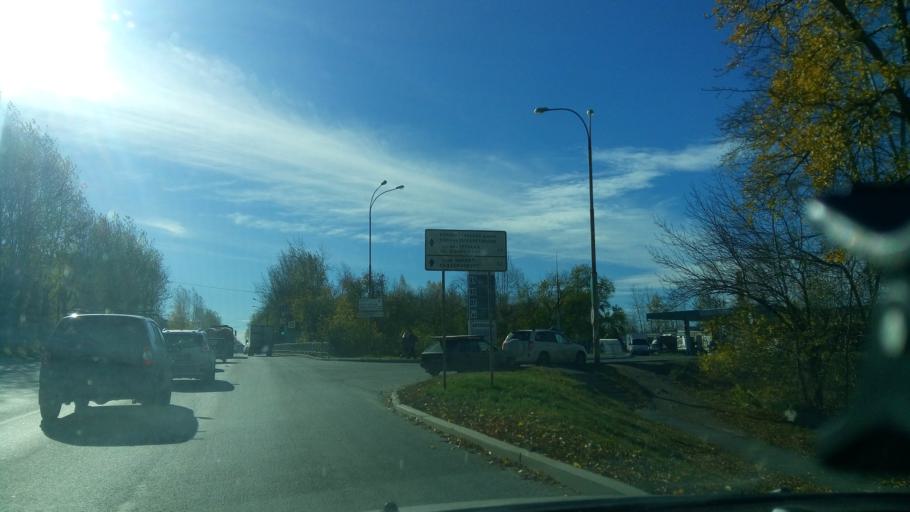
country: RU
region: Sverdlovsk
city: Sovkhoznyy
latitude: 56.7682
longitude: 60.6284
